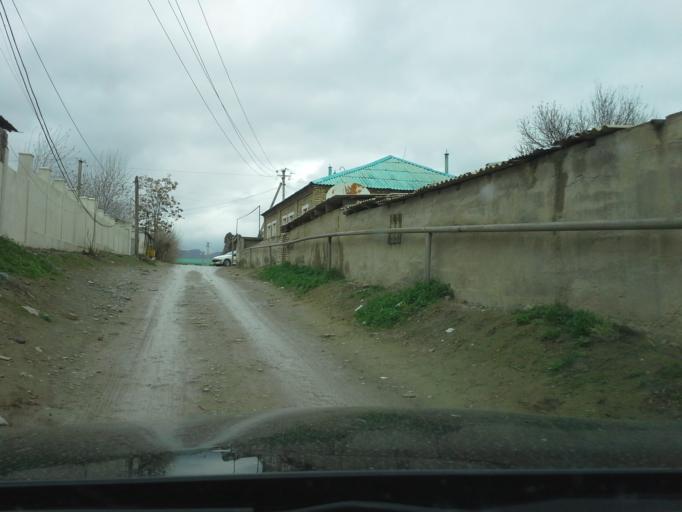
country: TM
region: Ahal
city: Abadan
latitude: 37.9572
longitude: 58.2102
